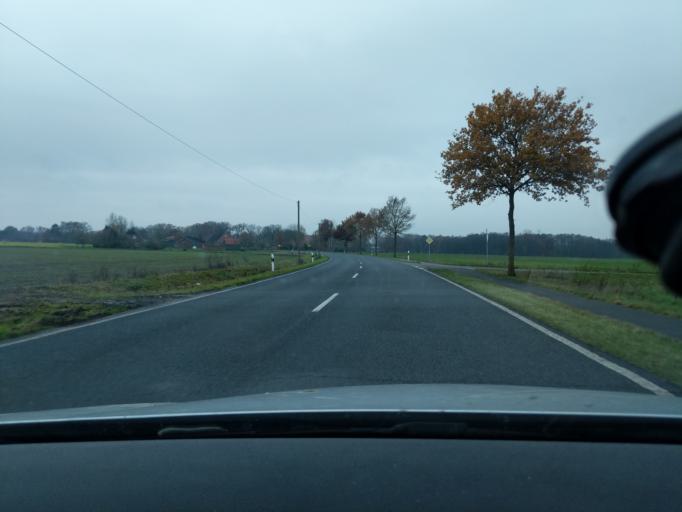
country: DE
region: Lower Saxony
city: Ahlerstedt
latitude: 53.3552
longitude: 9.4064
